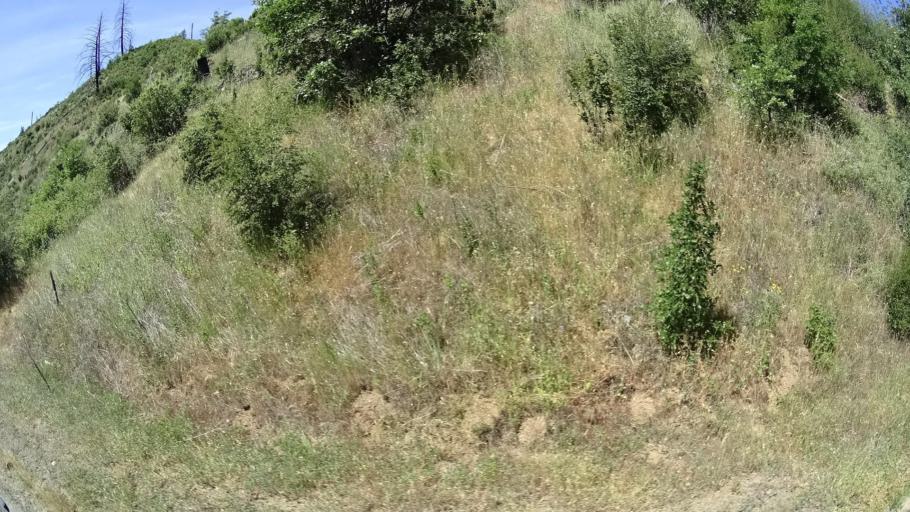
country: US
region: California
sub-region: Lake County
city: Middletown
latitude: 38.7791
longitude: -122.6305
